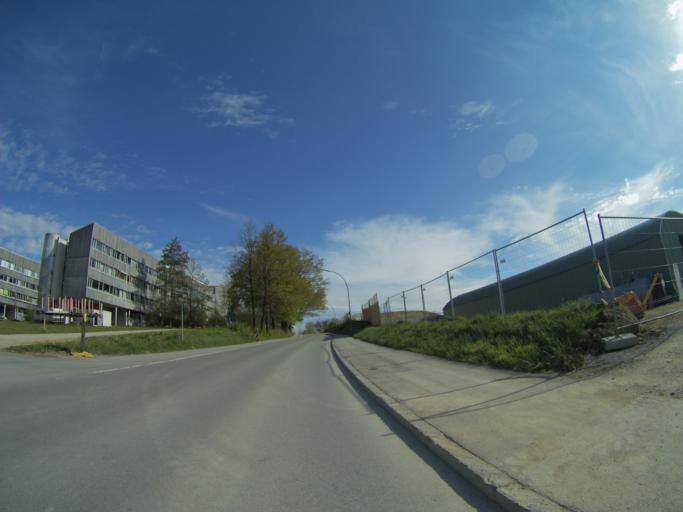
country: DE
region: Bavaria
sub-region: Upper Bavaria
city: Freising
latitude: 48.4013
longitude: 11.7154
